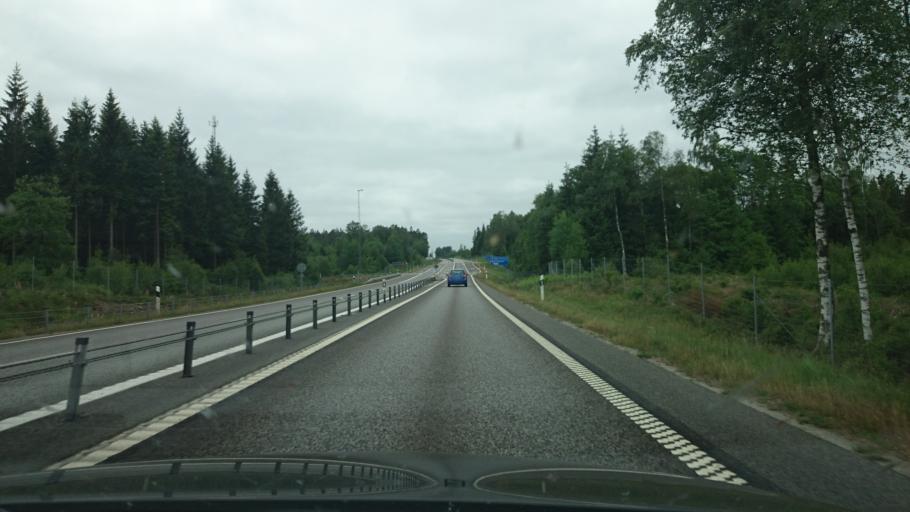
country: SE
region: Halland
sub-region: Hylte Kommun
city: Torup
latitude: 56.9700
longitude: 13.1450
